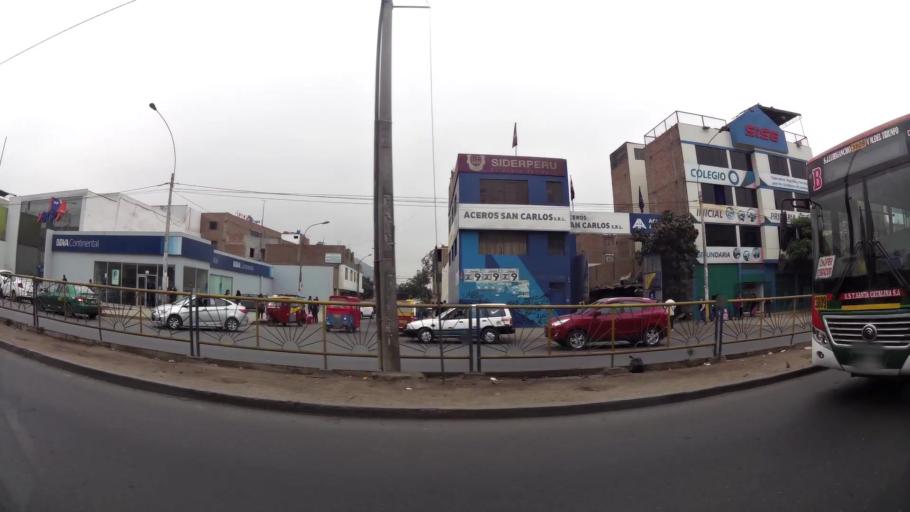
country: PE
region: Lima
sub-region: Lima
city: Independencia
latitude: -11.9872
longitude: -77.0079
